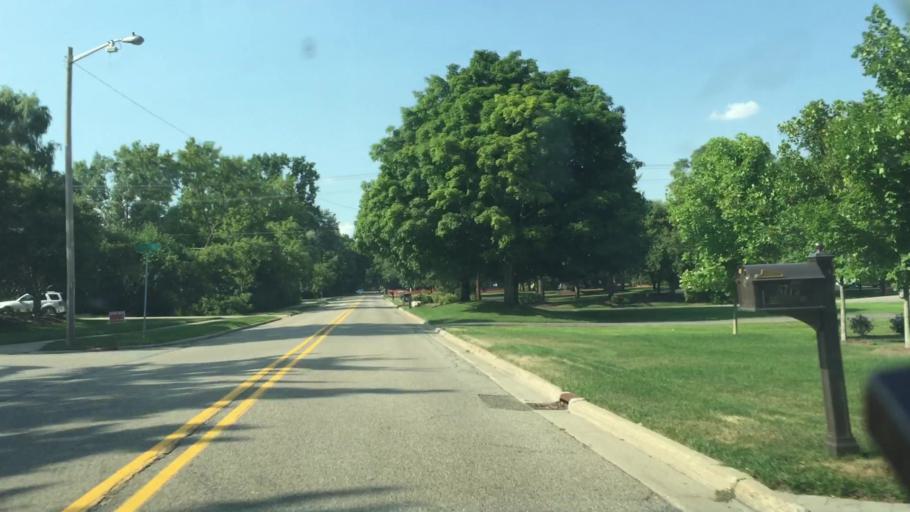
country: US
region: Michigan
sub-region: Oakland County
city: Franklin
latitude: 42.5408
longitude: -83.2968
